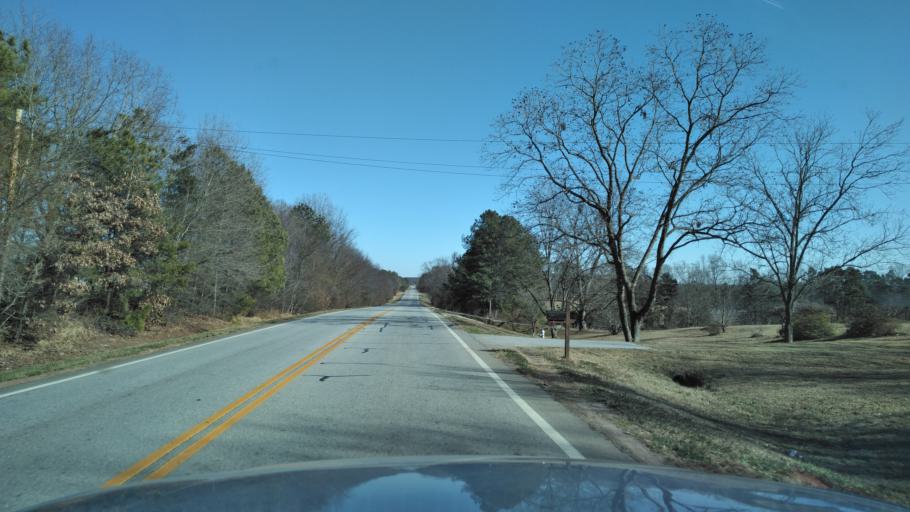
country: US
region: Georgia
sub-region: Banks County
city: Maysville
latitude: 34.2439
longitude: -83.5428
